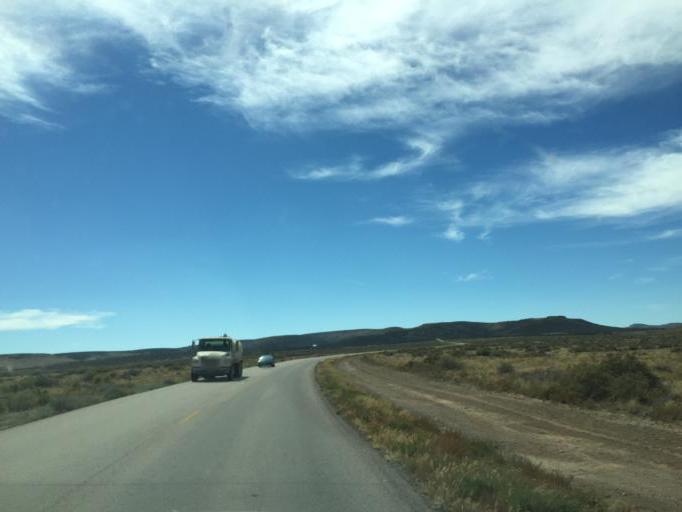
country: US
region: Arizona
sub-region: Mohave County
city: Meadview
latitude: 35.9488
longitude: -113.8508
